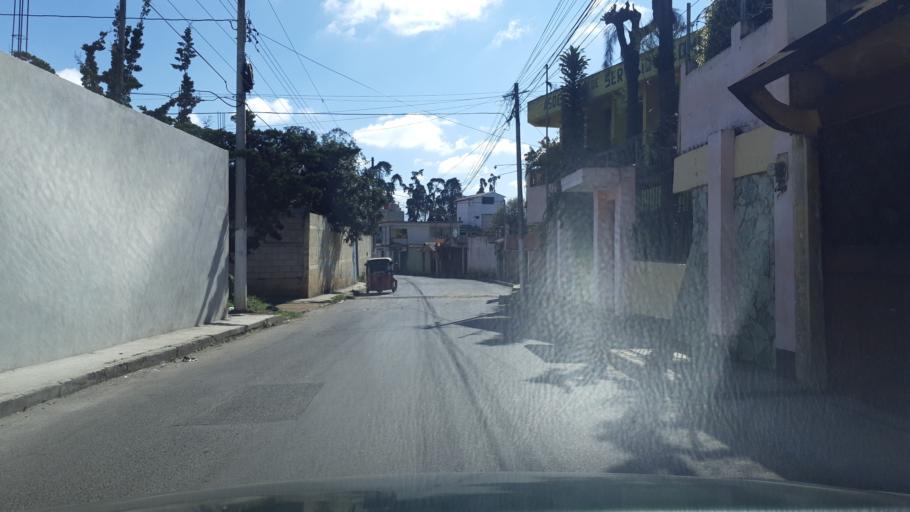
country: GT
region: Chimaltenango
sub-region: Municipio de Chimaltenango
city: Chimaltenango
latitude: 14.6553
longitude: -90.8175
